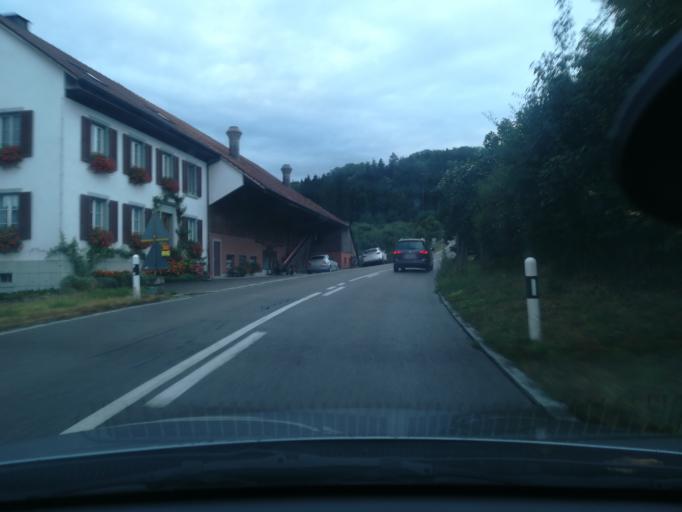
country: CH
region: Thurgau
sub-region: Frauenfeld District
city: Huttwilen
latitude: 47.6263
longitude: 8.8791
